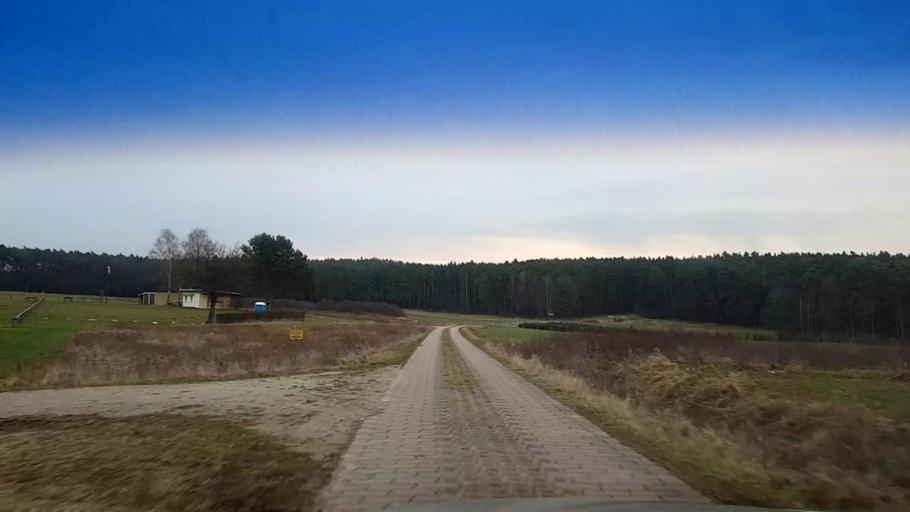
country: DE
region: Bavaria
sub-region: Upper Franconia
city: Pommersfelden
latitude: 49.8085
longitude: 10.8221
